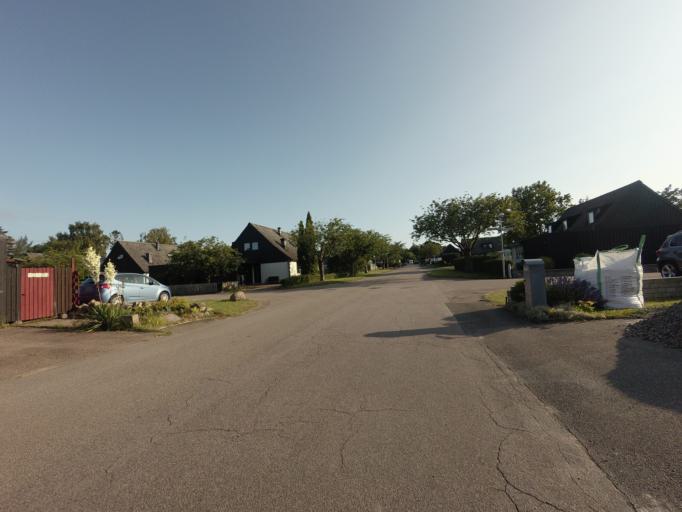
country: SE
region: Skane
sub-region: Landskrona
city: Asmundtorp
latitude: 55.8486
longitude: 12.9209
